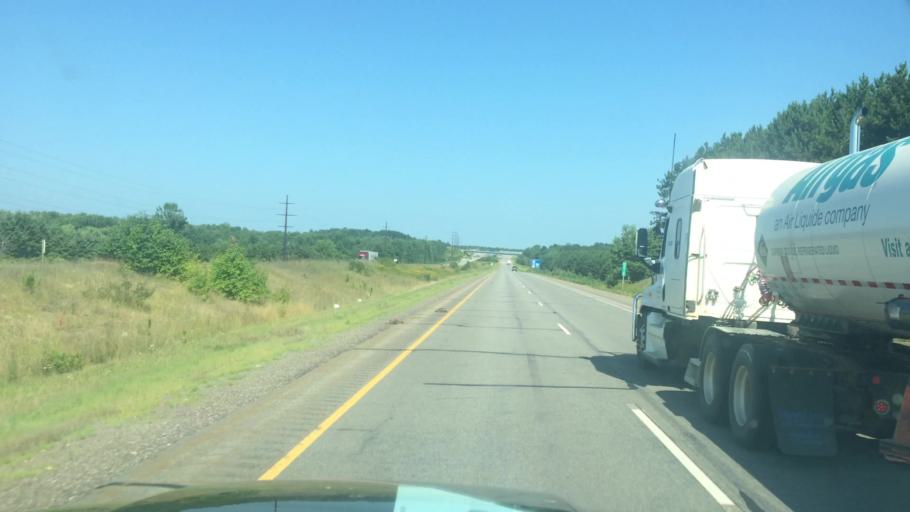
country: US
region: Wisconsin
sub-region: Lincoln County
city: Merrill
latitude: 45.1998
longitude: -89.6521
